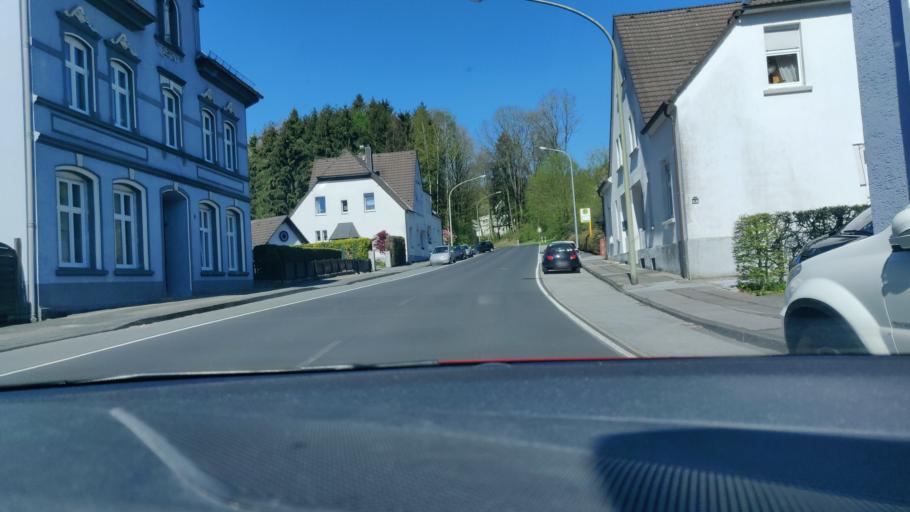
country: DE
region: North Rhine-Westphalia
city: Wulfrath
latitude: 51.2873
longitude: 7.0642
